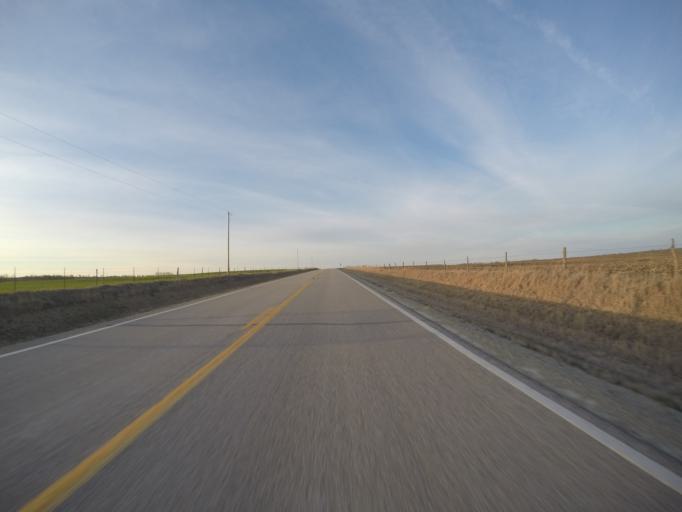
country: US
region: Kansas
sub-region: Clay County
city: Clay Center
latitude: 39.3900
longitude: -96.8492
